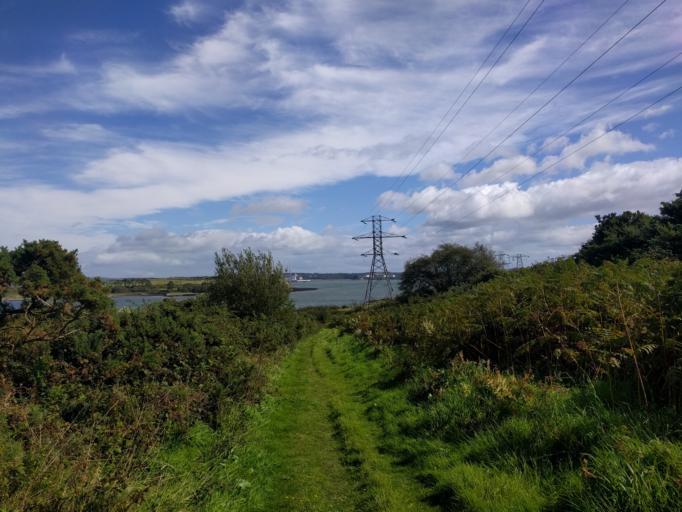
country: IE
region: Munster
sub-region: County Cork
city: Cobh
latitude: 51.8294
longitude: -8.3040
